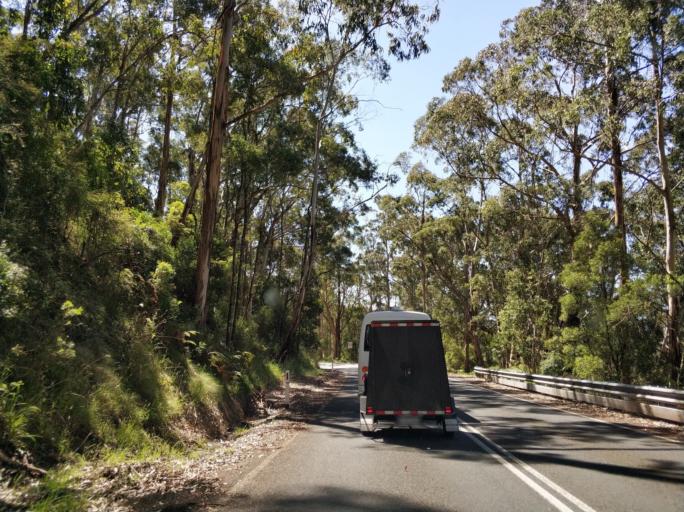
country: AU
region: Victoria
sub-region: Colac-Otway
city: Apollo Bay
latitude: -38.7391
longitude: 143.2523
